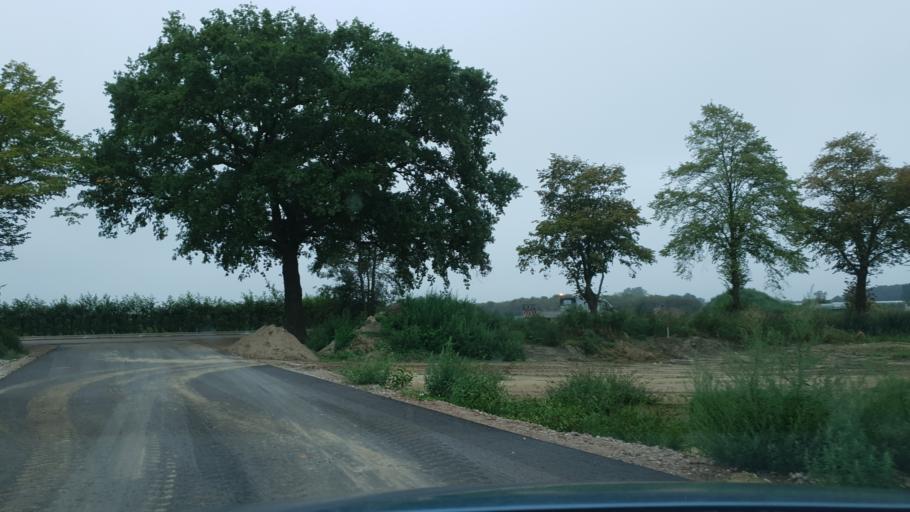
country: NL
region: Limburg
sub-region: Gemeente Peel en Maas
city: Maasbree
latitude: 51.4094
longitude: 6.0666
